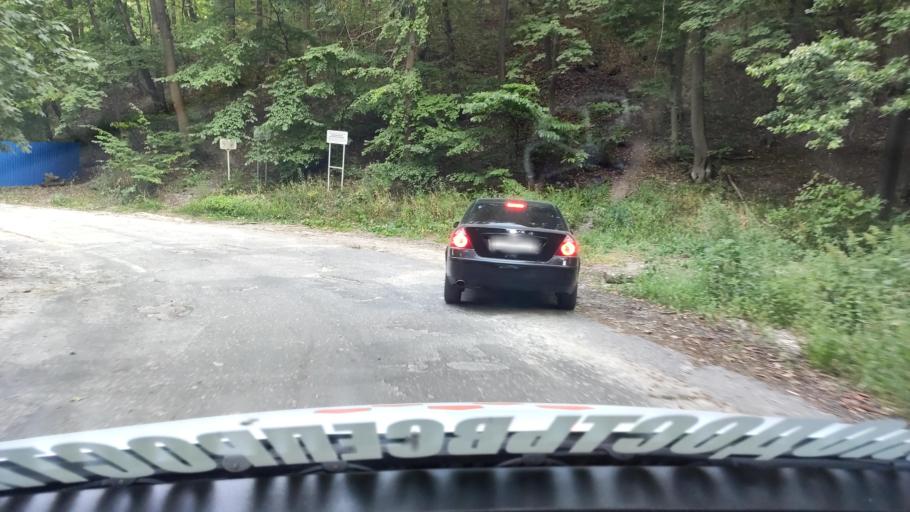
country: RU
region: Voronezj
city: Podgornoye
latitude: 51.7419
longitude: 39.2246
